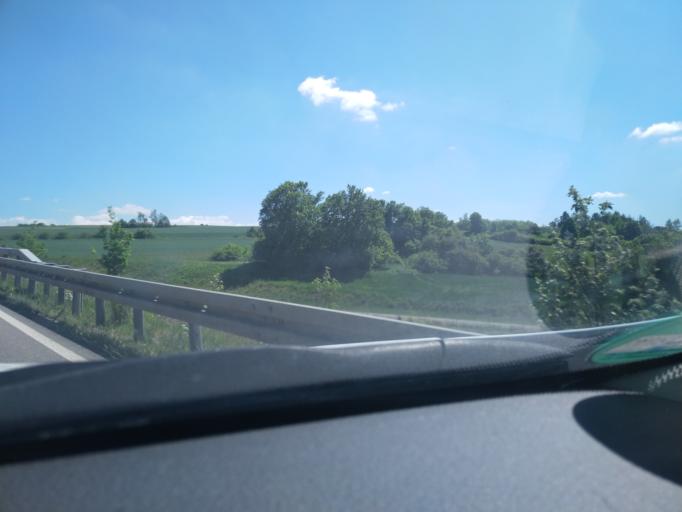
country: DE
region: Baden-Wuerttemberg
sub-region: Freiburg Region
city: Dunningen
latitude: 48.2181
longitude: 8.5140
